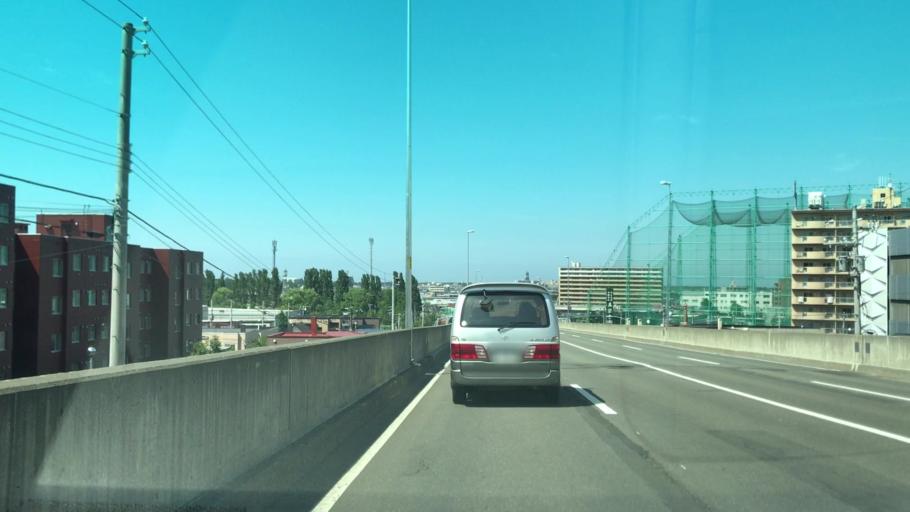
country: JP
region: Hokkaido
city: Sapporo
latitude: 43.1218
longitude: 141.2360
